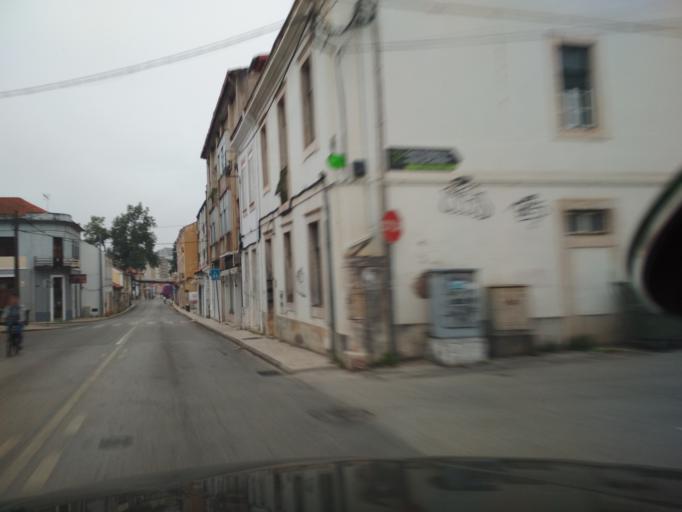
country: PT
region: Coimbra
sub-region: Coimbra
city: Coimbra
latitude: 40.2006
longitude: -8.4058
